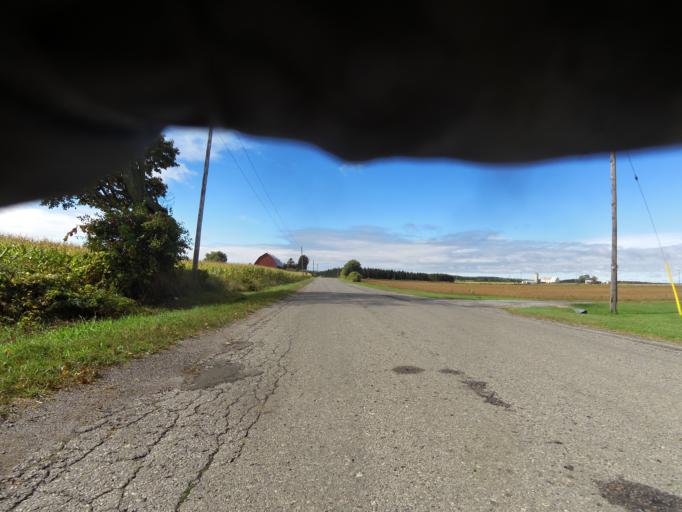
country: CA
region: Ontario
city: Cobourg
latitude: 43.9381
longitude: -78.3537
